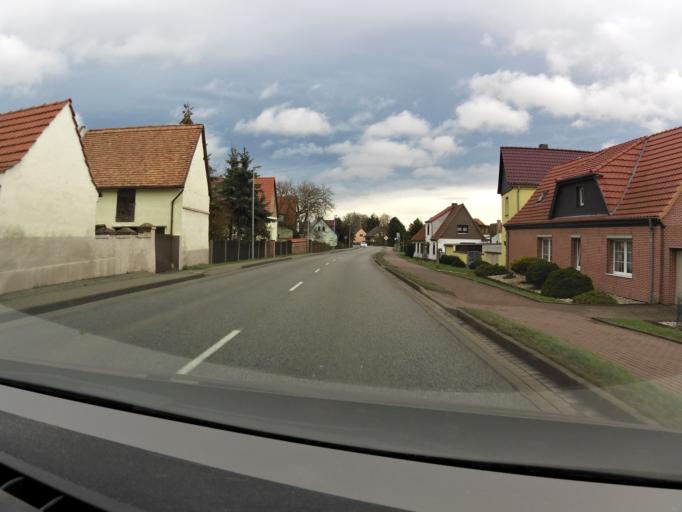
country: DE
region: Saxony-Anhalt
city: Blankenheim
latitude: 51.5503
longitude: 11.3995
